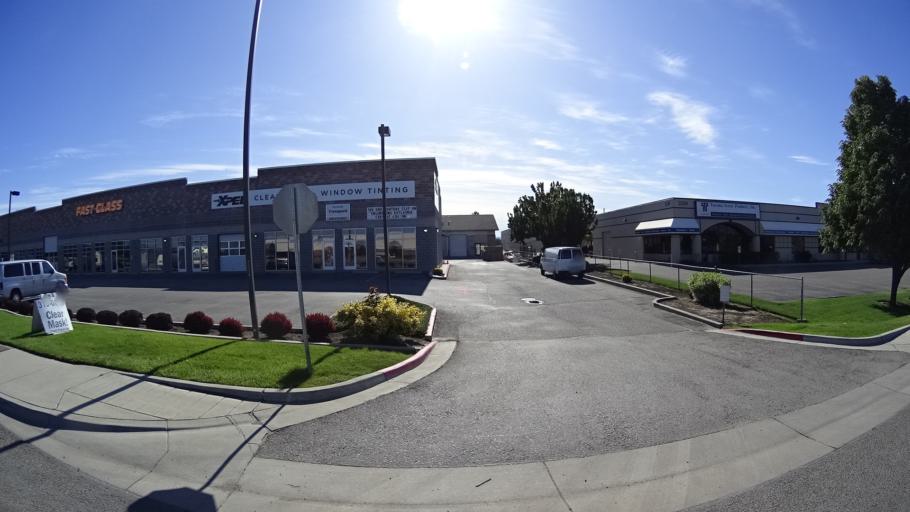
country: US
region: Idaho
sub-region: Ada County
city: Garden City
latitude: 43.5812
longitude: -116.2740
